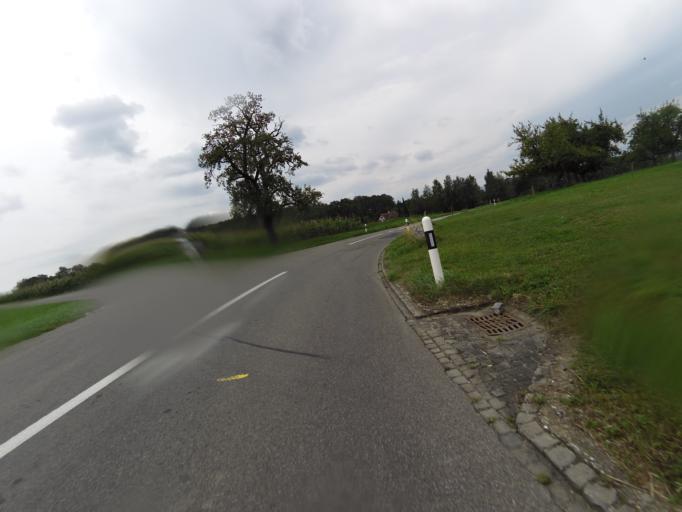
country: CH
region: Thurgau
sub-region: Weinfelden District
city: Wigoltingen
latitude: 47.6163
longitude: 9.0419
